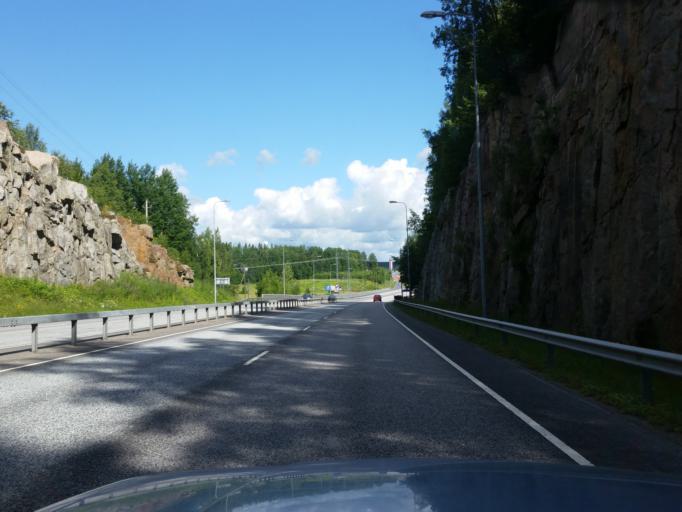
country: FI
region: Uusimaa
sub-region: Helsinki
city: Vihti
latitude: 60.3251
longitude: 24.3374
